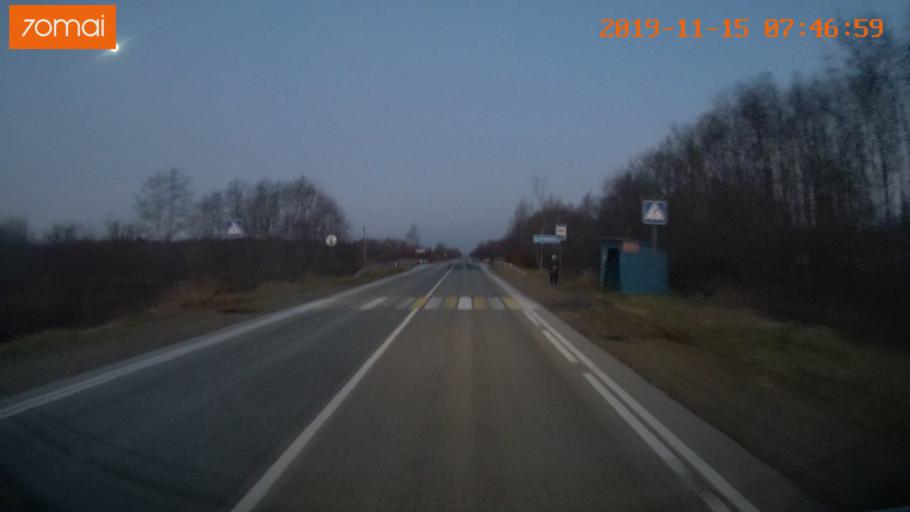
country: RU
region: Vologda
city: Sheksna
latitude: 58.8364
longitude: 38.2714
